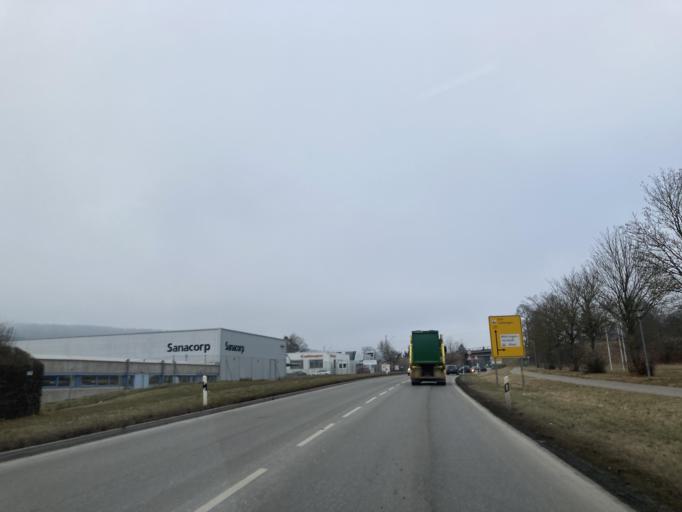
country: DE
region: Baden-Wuerttemberg
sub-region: Freiburg Region
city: Wurmlingen
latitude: 47.9628
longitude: 8.7833
